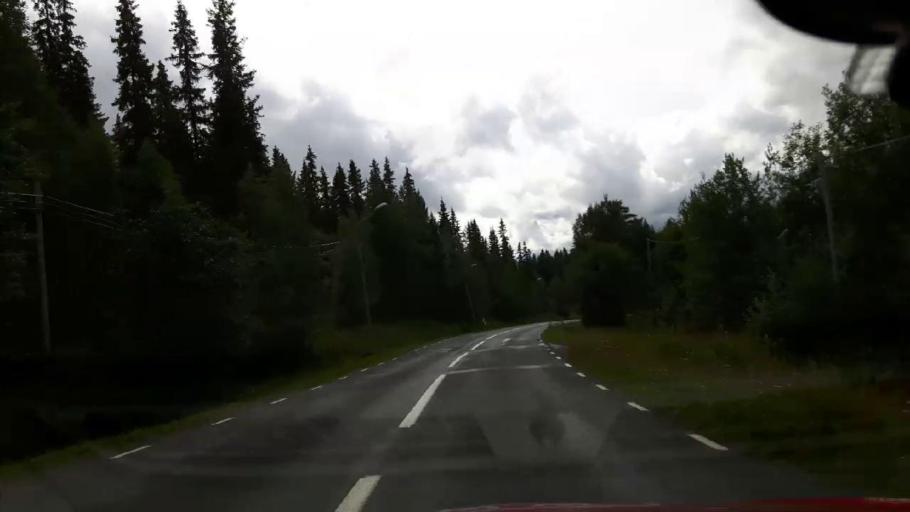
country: NO
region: Nord-Trondelag
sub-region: Lierne
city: Sandvika
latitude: 64.5027
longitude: 14.1566
